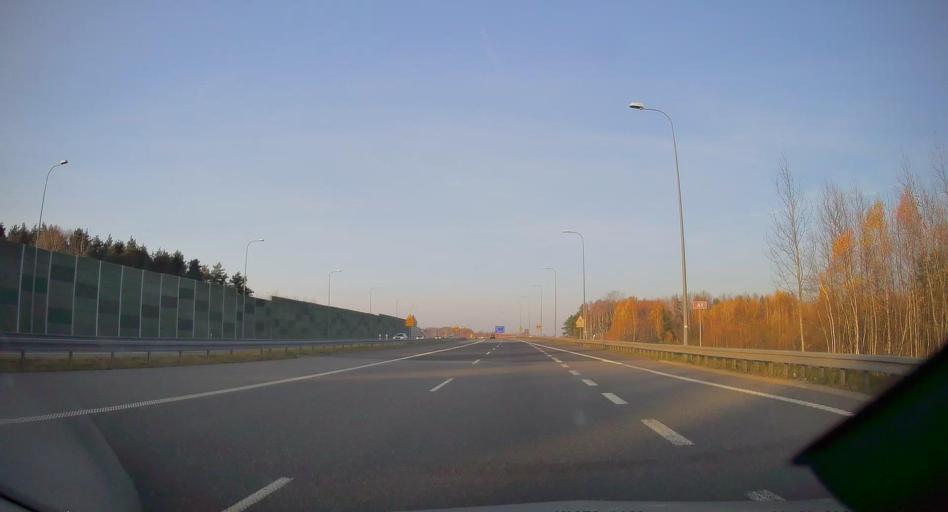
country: PL
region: Silesian Voivodeship
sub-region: Powiat tarnogorski
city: Ozarowice
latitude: 50.4604
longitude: 19.0571
